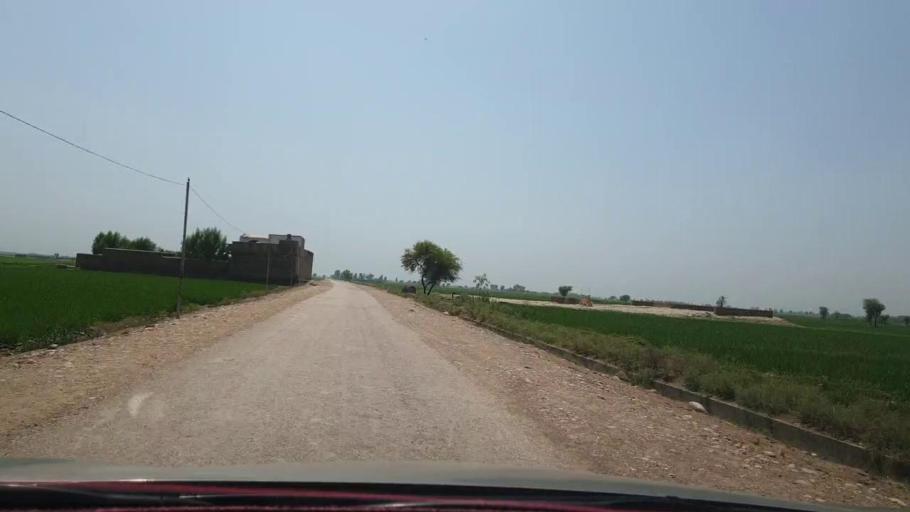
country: PK
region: Sindh
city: Warah
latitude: 27.5692
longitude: 67.8039
